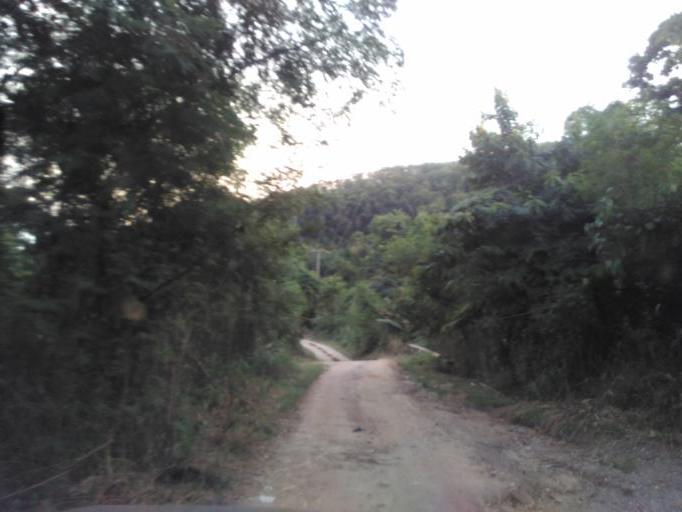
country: GH
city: Bekwai
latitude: 6.5356
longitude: -1.4323
